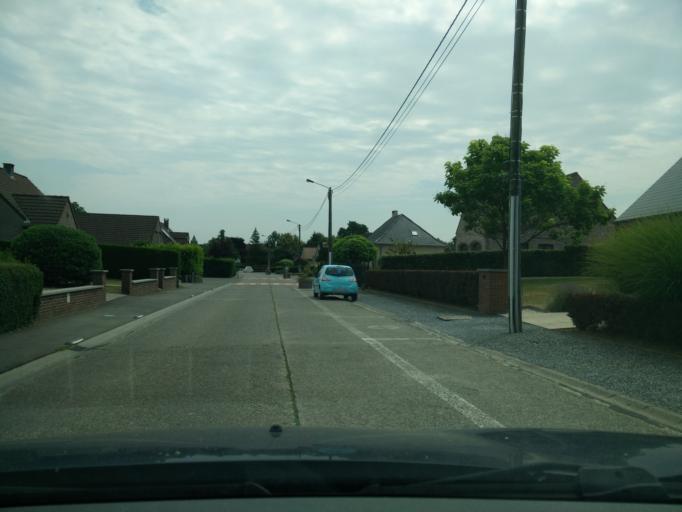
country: BE
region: Wallonia
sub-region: Province du Hainaut
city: Soignies
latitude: 50.5555
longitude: 4.0930
